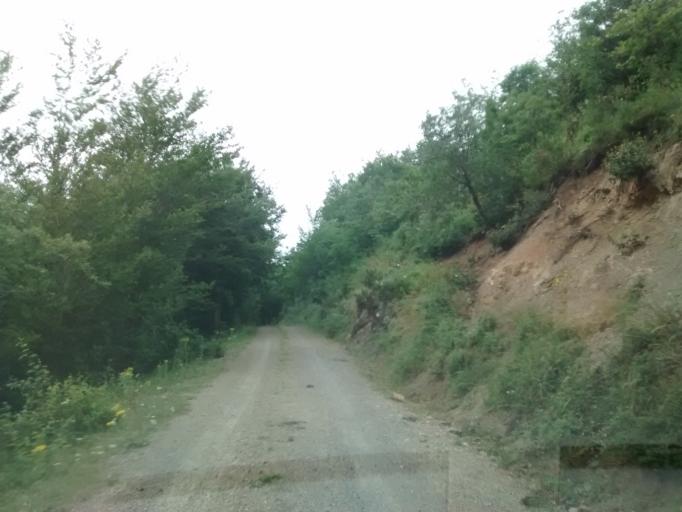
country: ES
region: La Rioja
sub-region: Provincia de La Rioja
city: Ajamil
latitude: 42.1357
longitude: -2.4820
